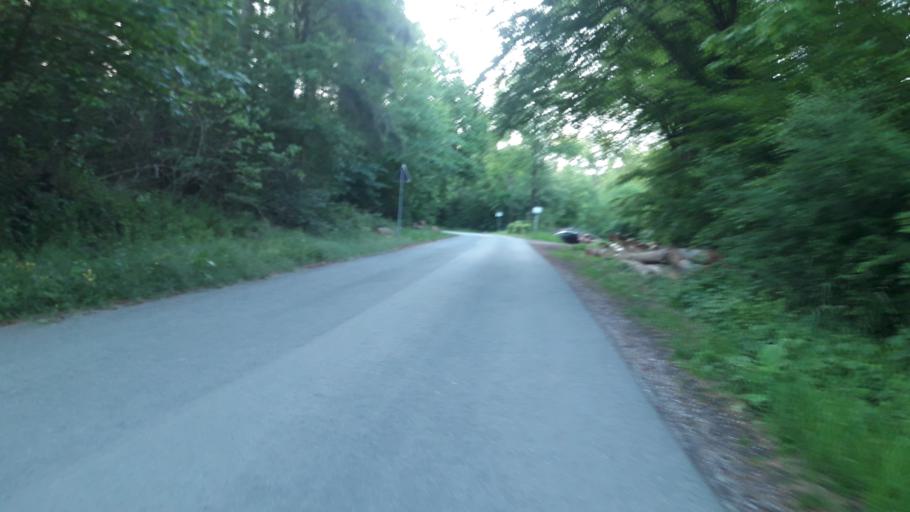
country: DE
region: North Rhine-Westphalia
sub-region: Regierungsbezirk Detmold
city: Paderborn
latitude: 51.6650
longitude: 8.7696
